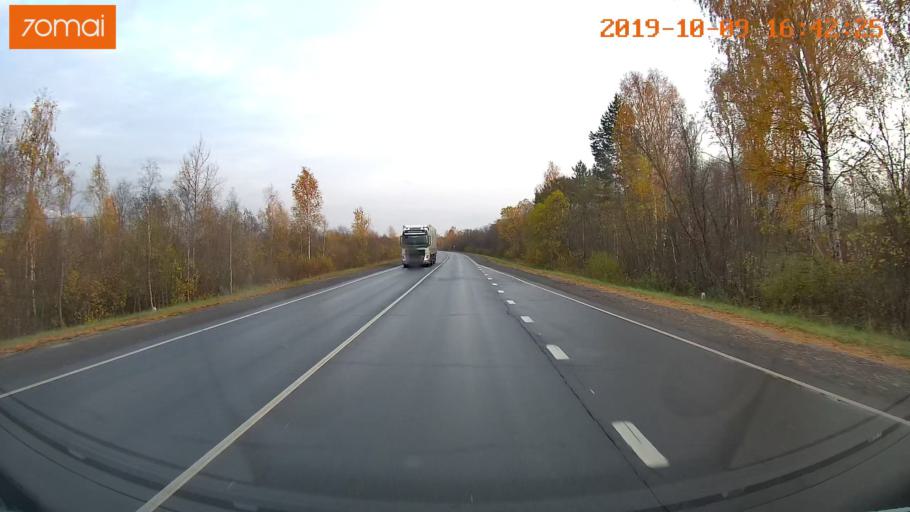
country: RU
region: Kostroma
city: Volgorechensk
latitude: 57.4623
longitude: 41.0998
